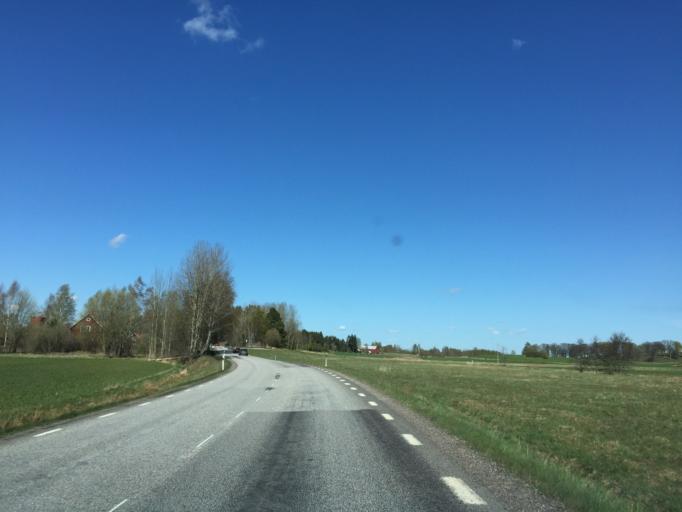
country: SE
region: OErebro
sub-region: Hallsbergs Kommun
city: Skollersta
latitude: 59.1185
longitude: 15.3317
